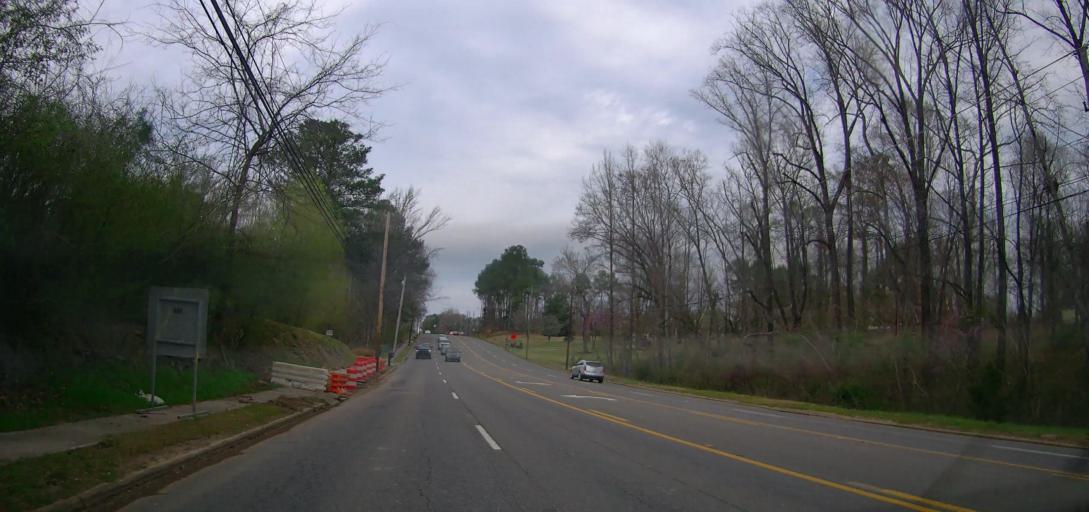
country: US
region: Alabama
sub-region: Marion County
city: Hamilton
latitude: 34.1294
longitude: -87.9900
